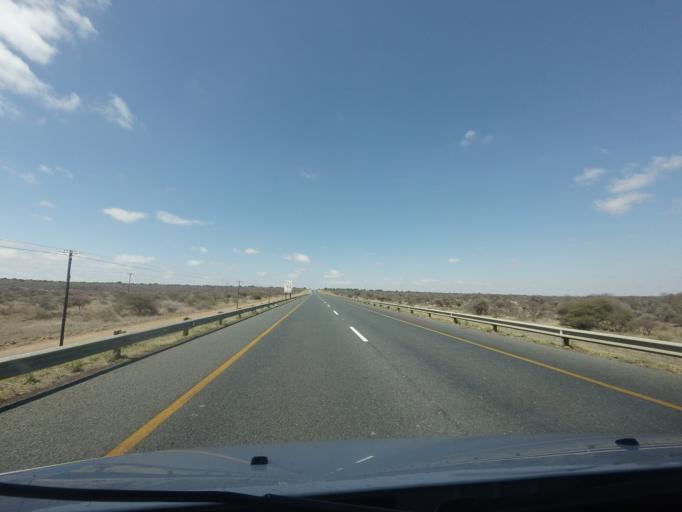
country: ZA
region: Limpopo
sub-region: Vhembe District Municipality
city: Louis Trichardt
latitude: -23.3926
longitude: 29.7623
